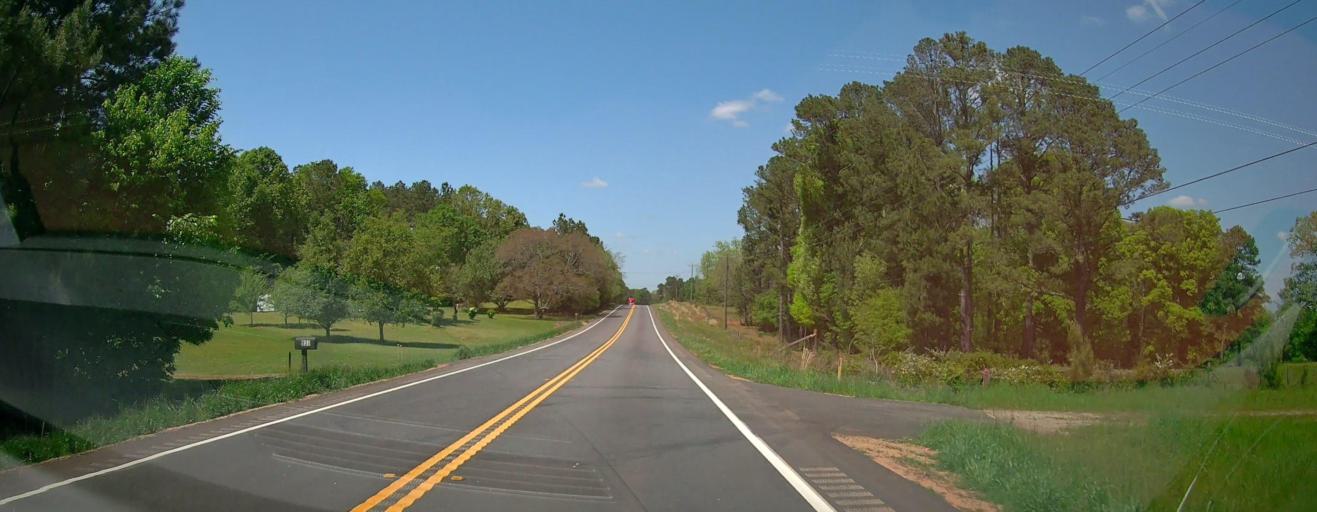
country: US
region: Georgia
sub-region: Putnam County
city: Eatonton
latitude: 33.2032
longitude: -83.4337
